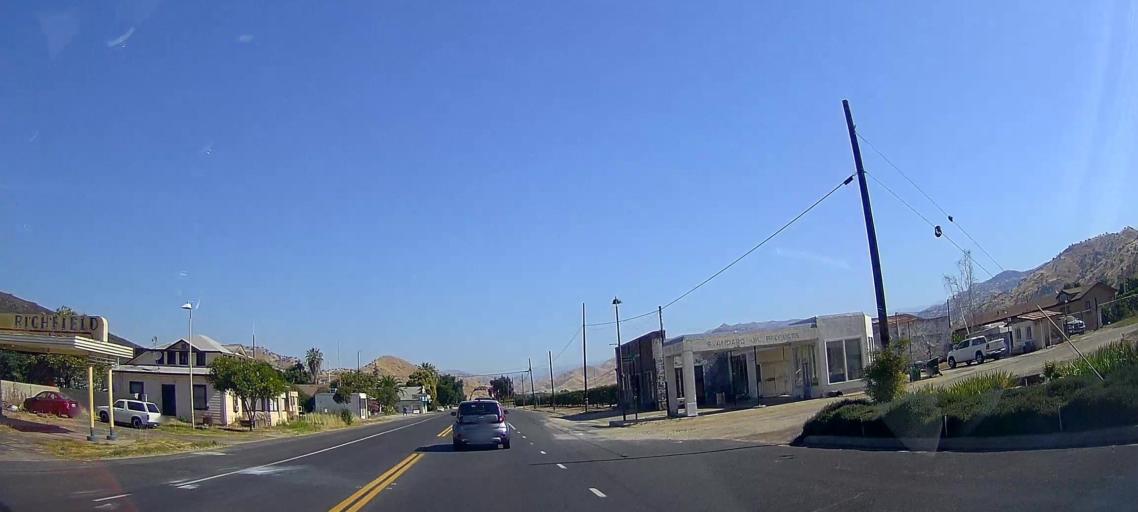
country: US
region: California
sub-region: Tulare County
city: Woodlake
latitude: 36.3828
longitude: -119.0243
